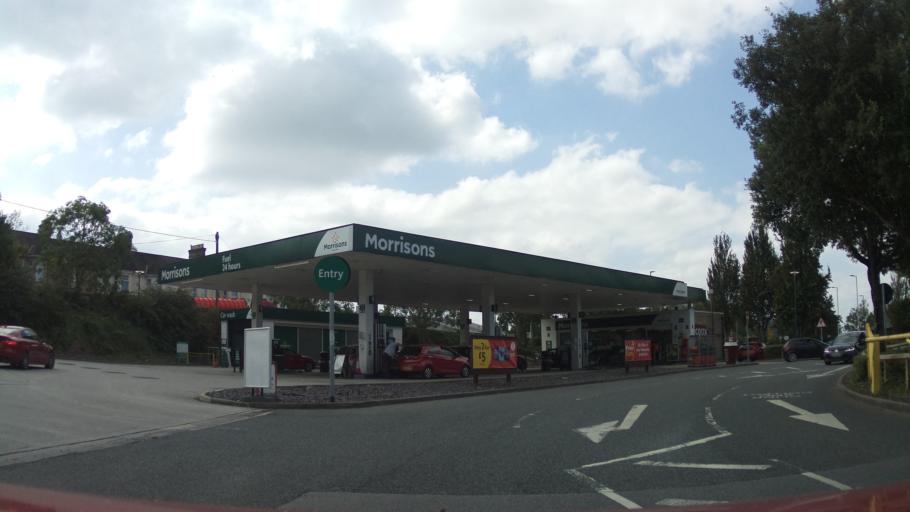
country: GB
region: England
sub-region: Plymouth
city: Plymstock
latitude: 50.3659
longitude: -4.0993
